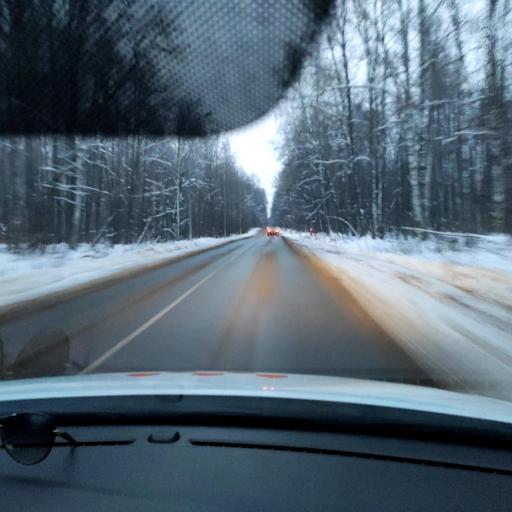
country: RU
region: Tatarstan
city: Vysokaya Gora
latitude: 55.9349
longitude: 49.1766
